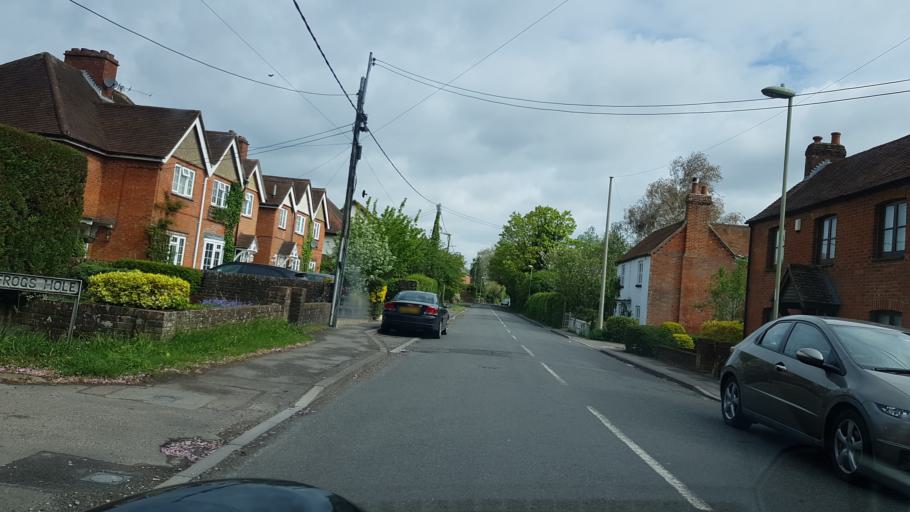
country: GB
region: England
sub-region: Hampshire
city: Kingsclere
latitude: 51.3268
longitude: -1.2510
